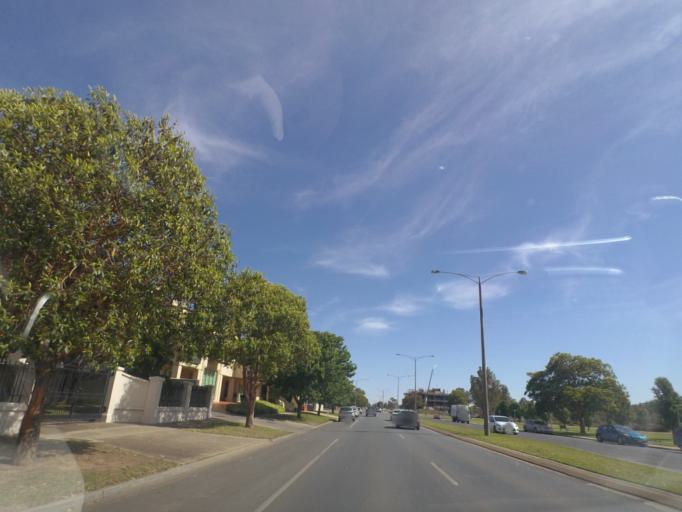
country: AU
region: Victoria
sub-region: Greater Shepparton
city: Shepparton
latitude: -36.3882
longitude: 145.3980
